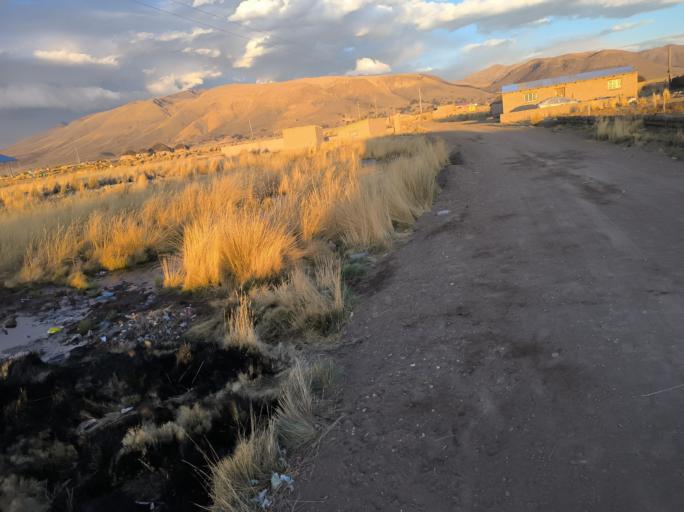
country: BO
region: Oruro
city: Challapata
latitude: -19.0095
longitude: -66.8204
